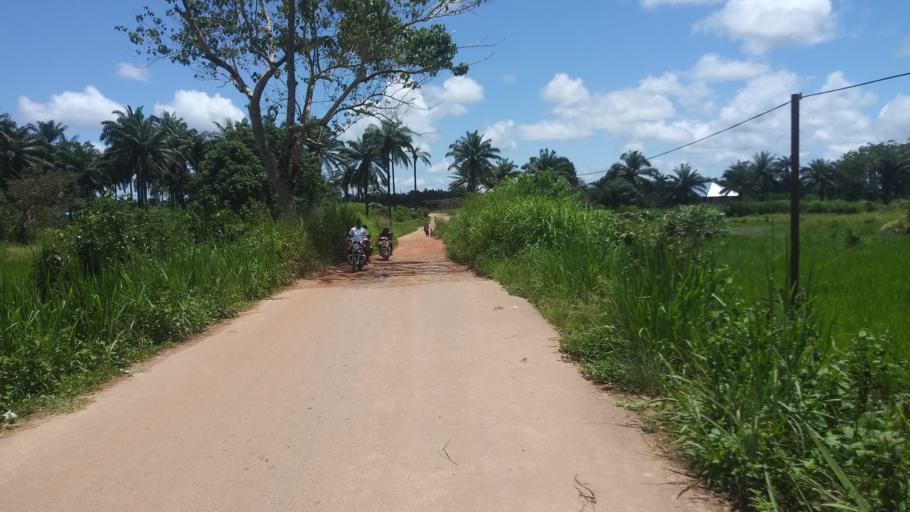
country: SL
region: Northern Province
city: Makeni
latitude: 8.8793
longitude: -12.0207
